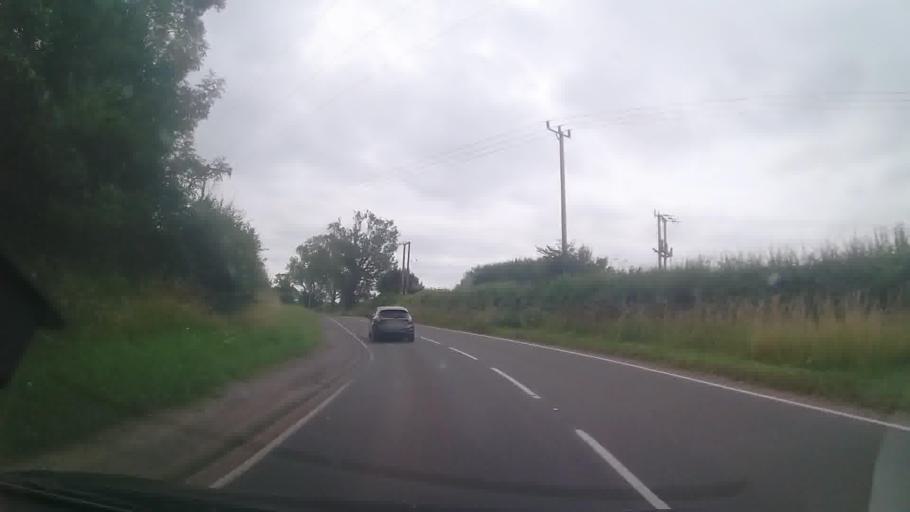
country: GB
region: England
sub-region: Leicestershire
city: Desford
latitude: 52.6367
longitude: -1.2820
